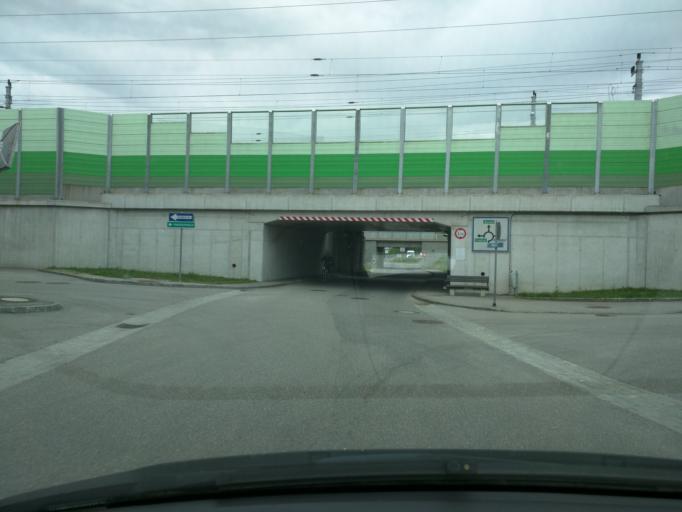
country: AT
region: Lower Austria
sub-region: Politischer Bezirk Melk
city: Blindenmarkt
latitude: 48.1258
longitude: 14.9873
